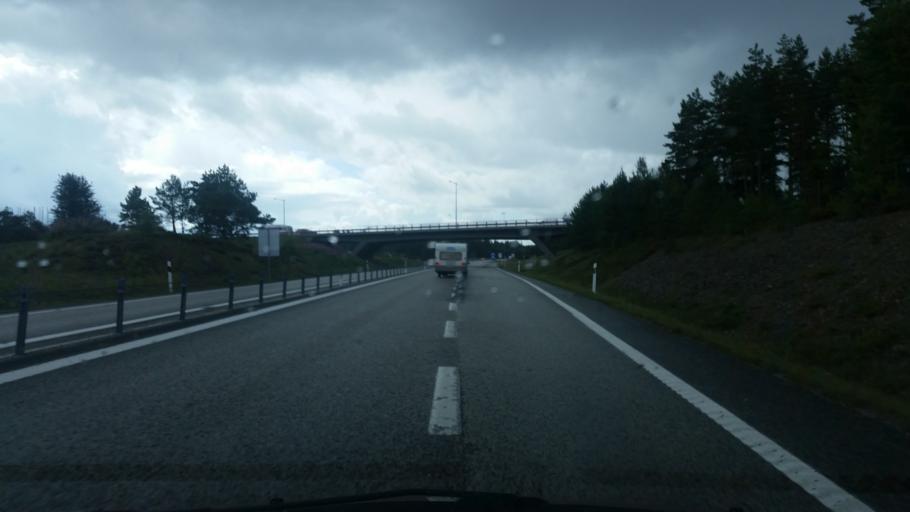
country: SE
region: Joenkoeping
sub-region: Gislaveds Kommun
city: Gislaved
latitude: 57.3257
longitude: 13.5448
